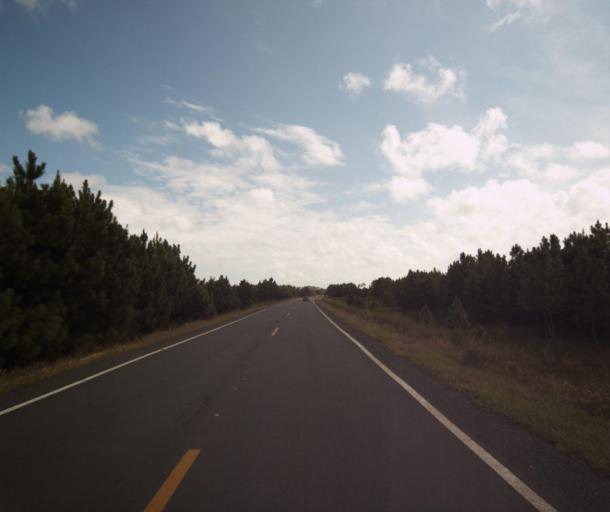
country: BR
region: Rio Grande do Sul
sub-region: Sao Lourenco Do Sul
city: Sao Lourenco do Sul
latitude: -31.4416
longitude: -51.2002
